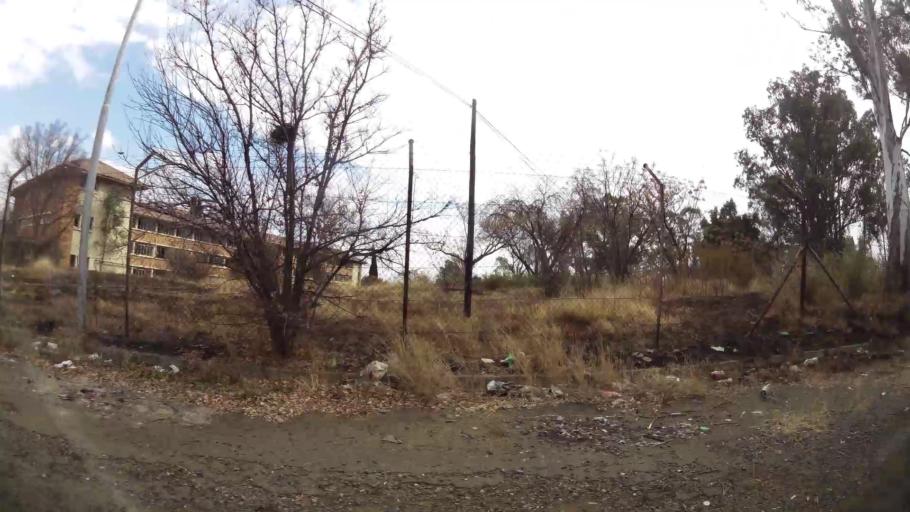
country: ZA
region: Orange Free State
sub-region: Fezile Dabi District Municipality
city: Kroonstad
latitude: -27.6537
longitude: 27.2332
